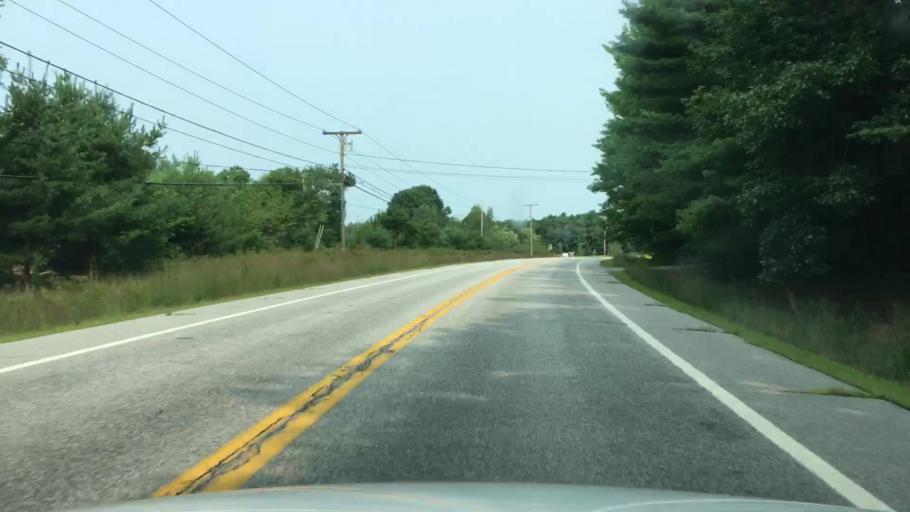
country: US
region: Maine
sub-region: Androscoggin County
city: Livermore Falls
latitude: 44.4147
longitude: -70.1447
